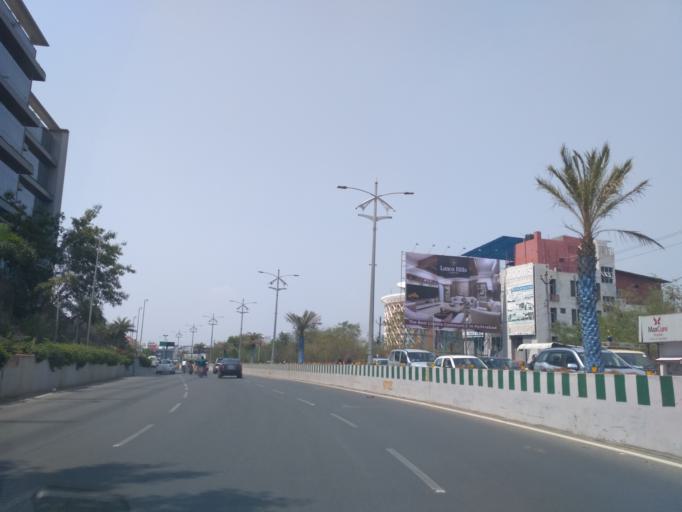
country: IN
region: Telangana
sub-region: Rangareddi
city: Kukatpalli
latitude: 17.4484
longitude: 78.3789
